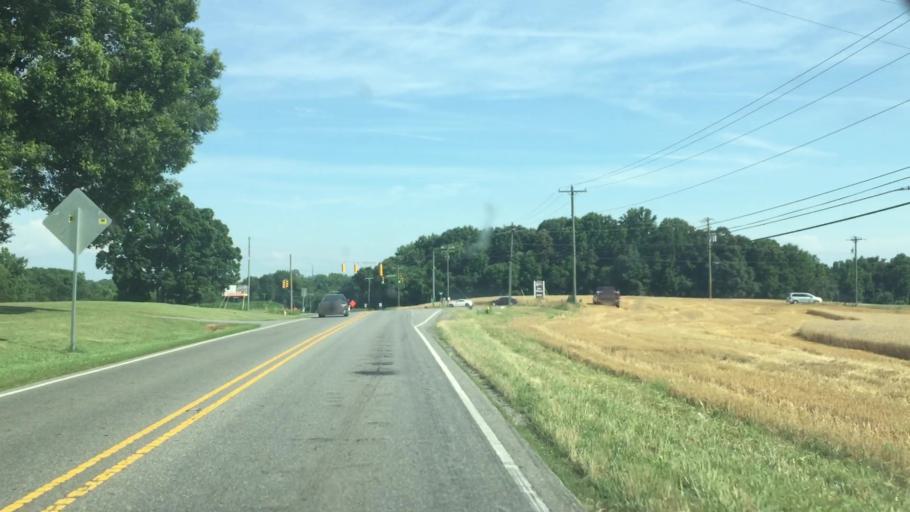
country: US
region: North Carolina
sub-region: Iredell County
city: Mooresville
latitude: 35.5621
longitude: -80.7890
